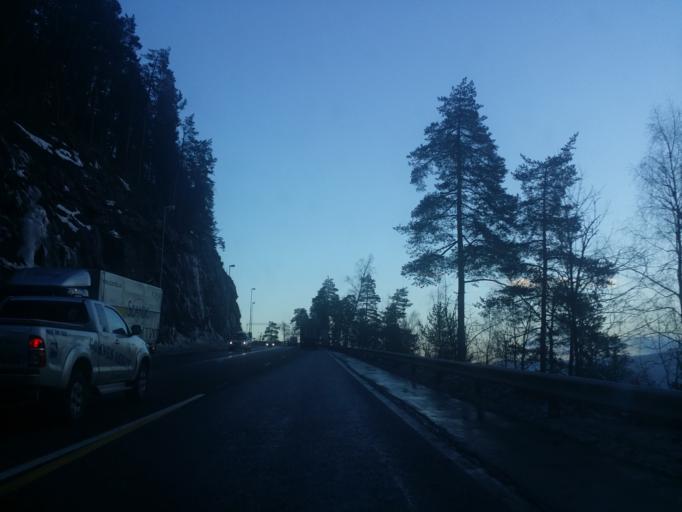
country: NO
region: Buskerud
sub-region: Hole
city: Vik
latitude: 59.9913
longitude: 10.3019
